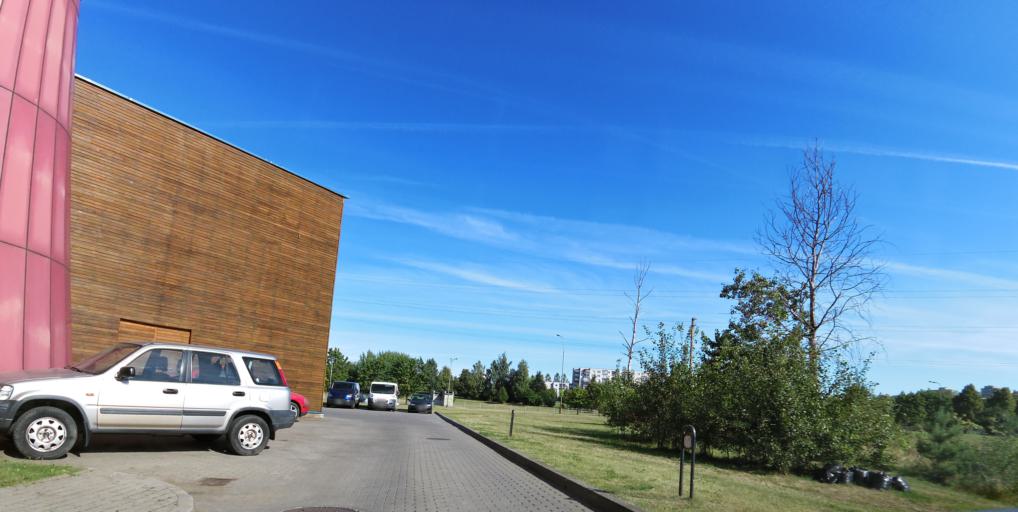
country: LT
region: Vilnius County
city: Seskine
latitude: 54.7084
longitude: 25.2420
